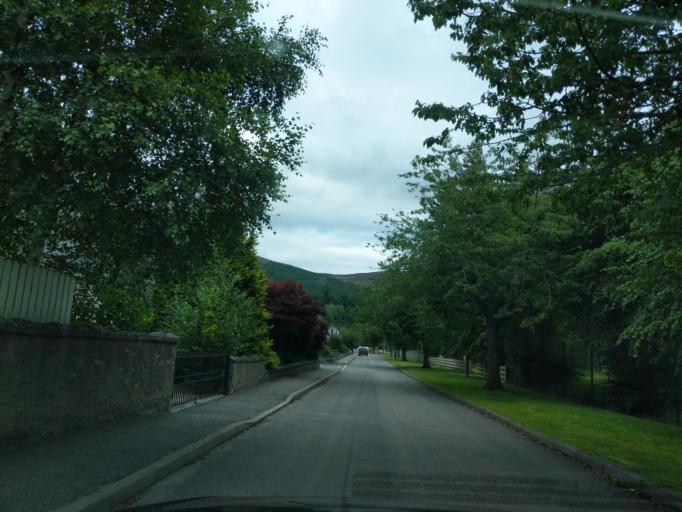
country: GB
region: Scotland
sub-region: Aberdeenshire
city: Ballater
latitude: 57.0461
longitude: -3.0437
